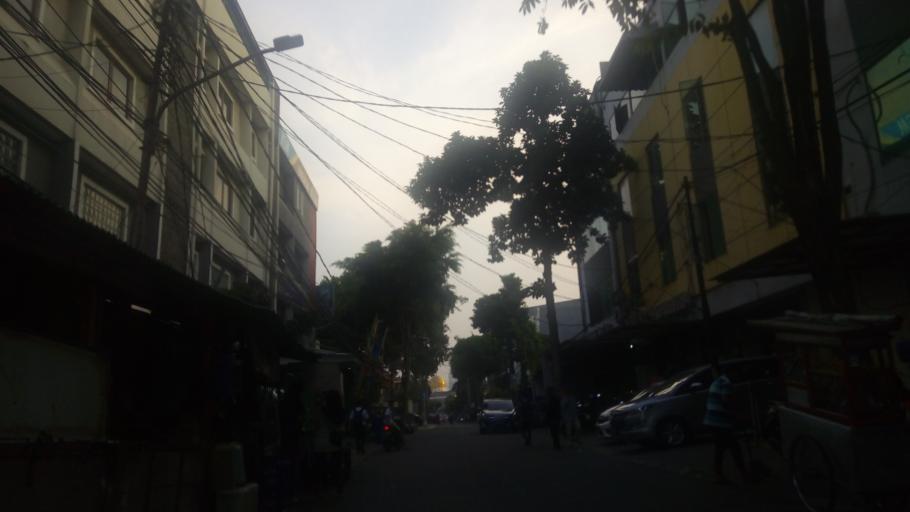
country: ID
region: Jakarta Raya
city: Jakarta
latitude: -6.1980
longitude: 106.8517
